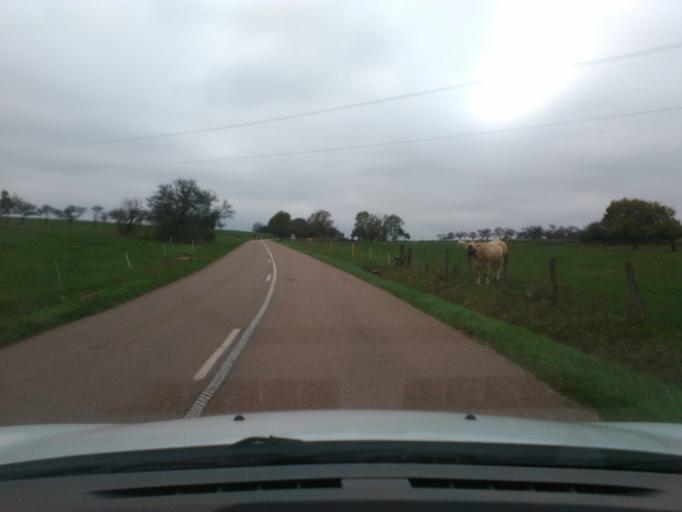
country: FR
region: Lorraine
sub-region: Departement des Vosges
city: Vincey
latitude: 48.3039
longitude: 6.3165
